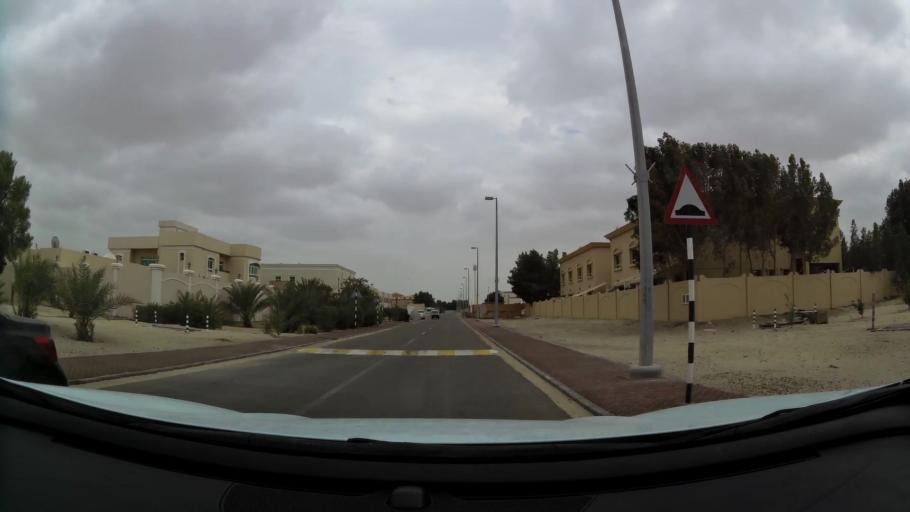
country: AE
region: Abu Dhabi
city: Abu Dhabi
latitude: 24.3775
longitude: 54.6383
